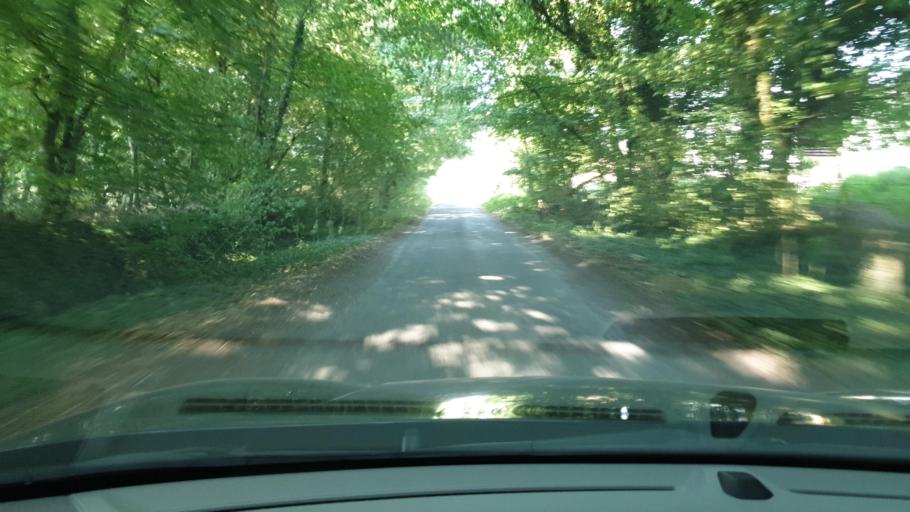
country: IE
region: Leinster
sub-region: An Mhi
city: Athboy
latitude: 53.6290
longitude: -6.9850
